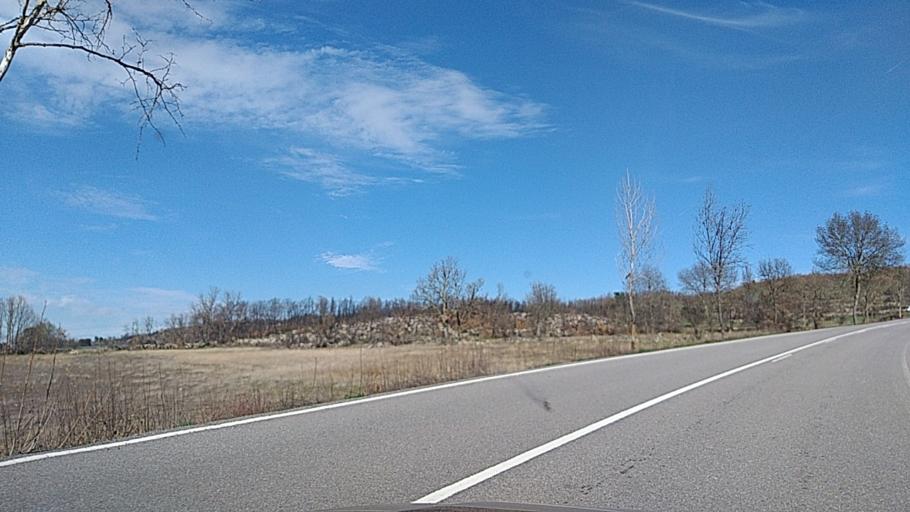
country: PT
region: Guarda
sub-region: Pinhel
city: Pinhel
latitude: 40.6010
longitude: -7.0276
